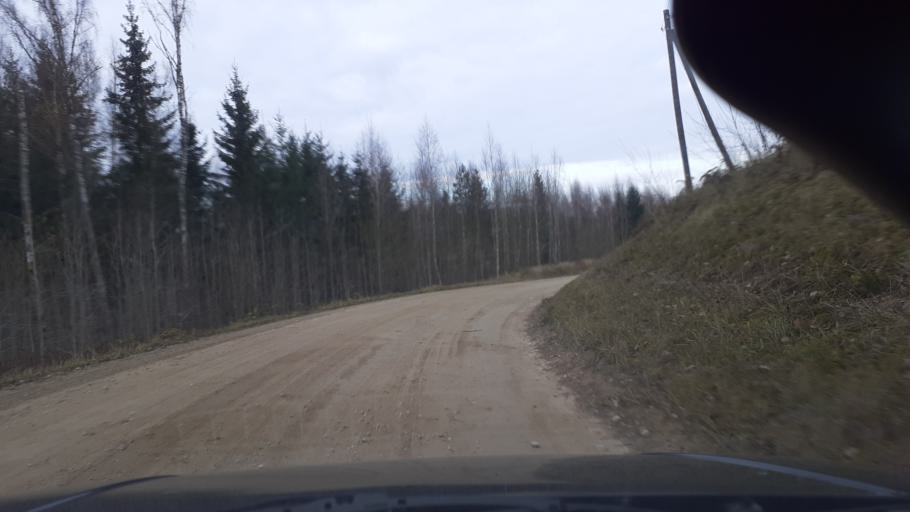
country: LV
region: Alsunga
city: Alsunga
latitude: 56.9868
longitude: 21.6697
